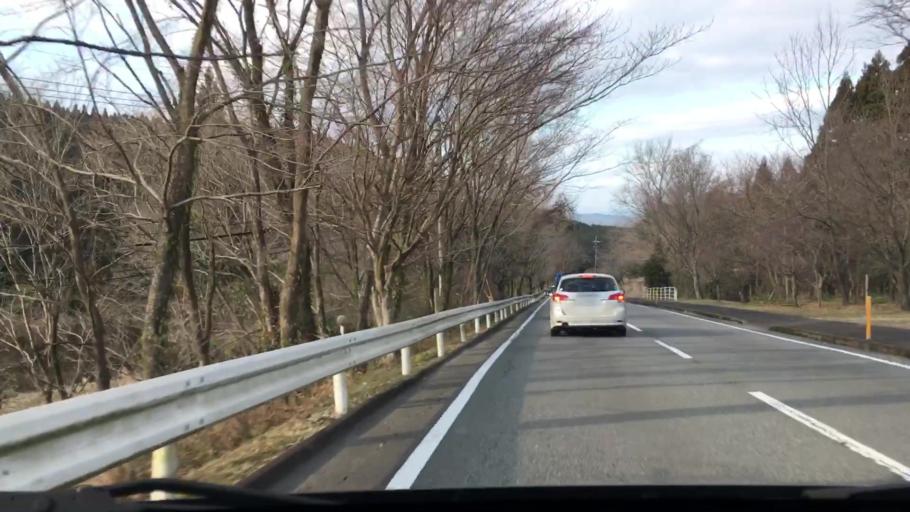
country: JP
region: Miyazaki
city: Miyazaki-shi
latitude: 31.8028
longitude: 131.3016
